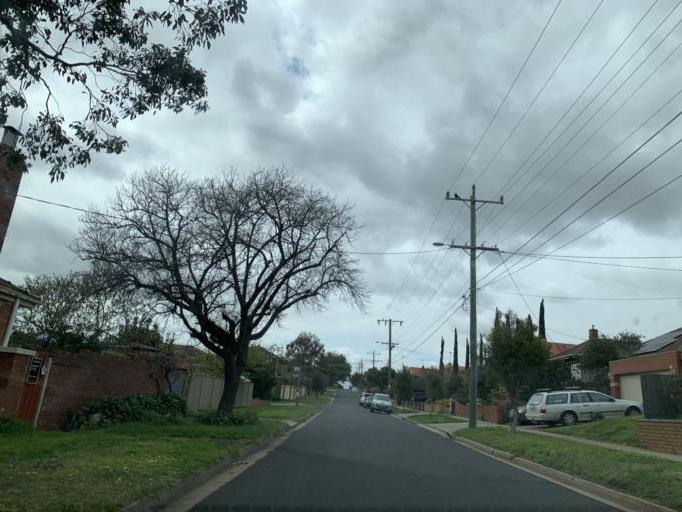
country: AU
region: Victoria
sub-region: Moreland
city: Pascoe Vale South
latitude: -37.7488
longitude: 144.9378
